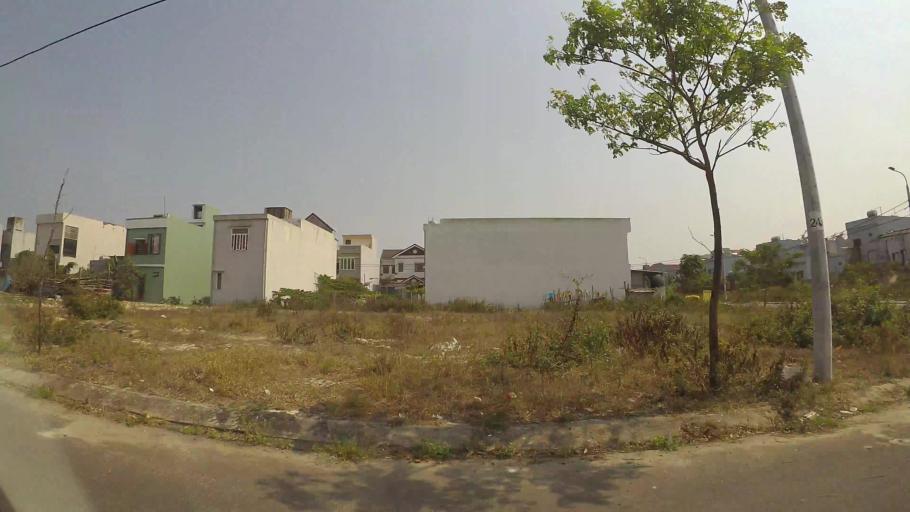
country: VN
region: Da Nang
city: Ngu Hanh Son
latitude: 15.9916
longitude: 108.2674
